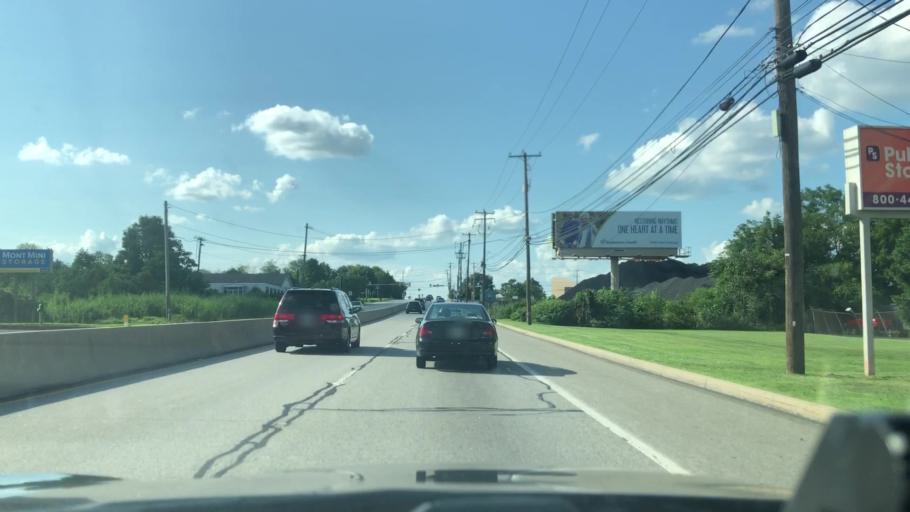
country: US
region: Pennsylvania
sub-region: Montgomery County
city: Spring House
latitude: 40.2149
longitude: -75.2274
